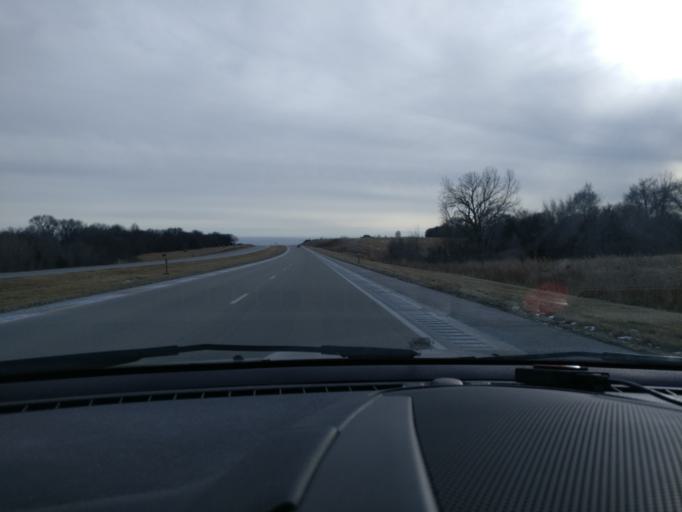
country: US
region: Nebraska
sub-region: Saunders County
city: Wahoo
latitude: 41.1829
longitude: -96.6336
